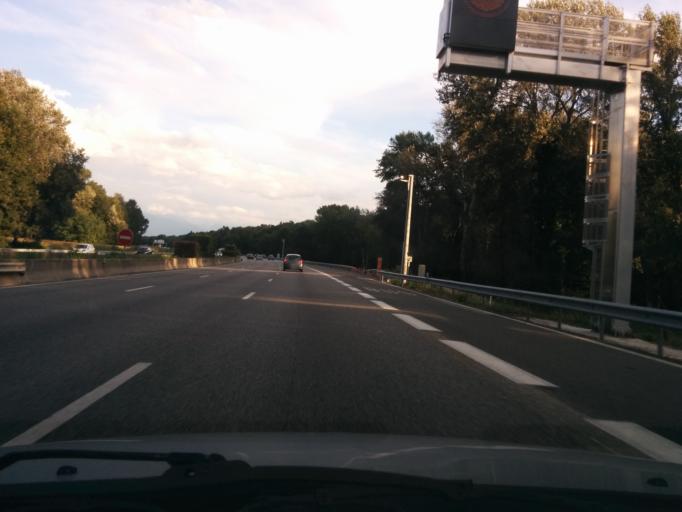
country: FR
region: Rhone-Alpes
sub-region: Departement de l'Isere
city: Veurey-Voroize
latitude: 45.2682
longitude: 5.6281
